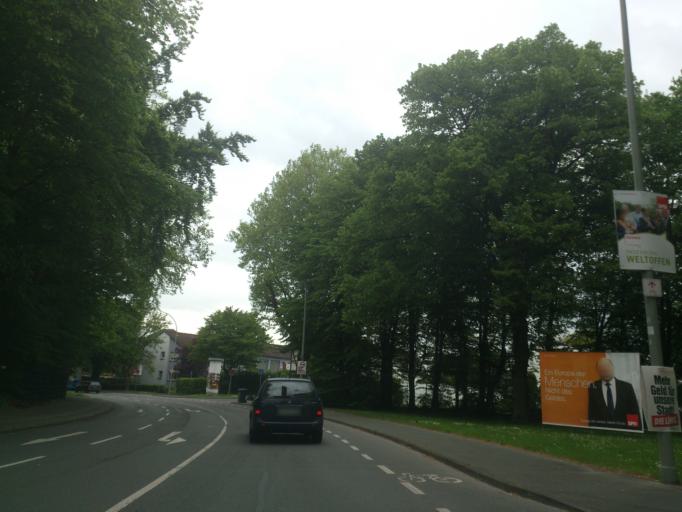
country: DE
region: North Rhine-Westphalia
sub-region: Regierungsbezirk Detmold
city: Paderborn
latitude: 51.7324
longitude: 8.7495
